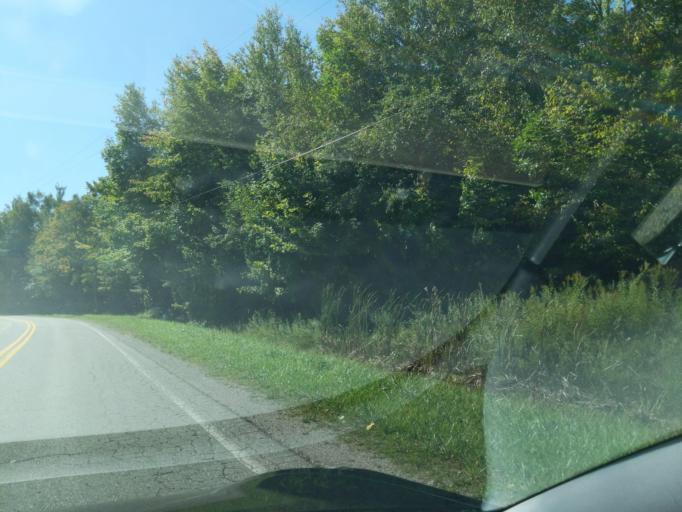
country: US
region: Michigan
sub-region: Antrim County
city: Elk Rapids
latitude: 44.9461
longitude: -85.3235
